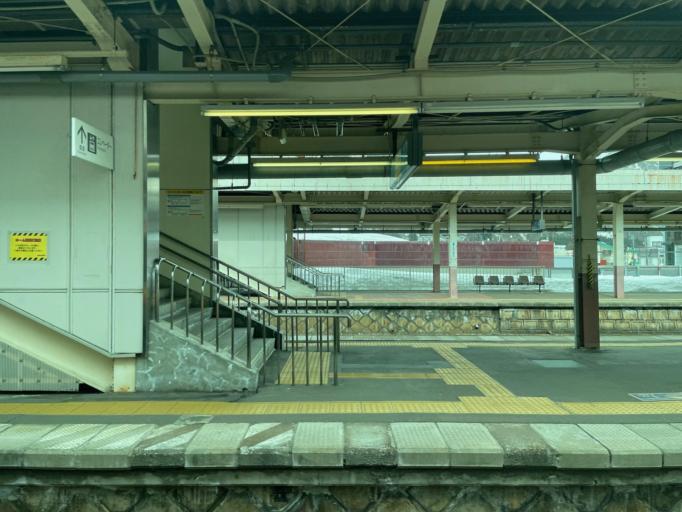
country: JP
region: Niigata
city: Shiozawa
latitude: 36.9359
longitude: 138.8101
